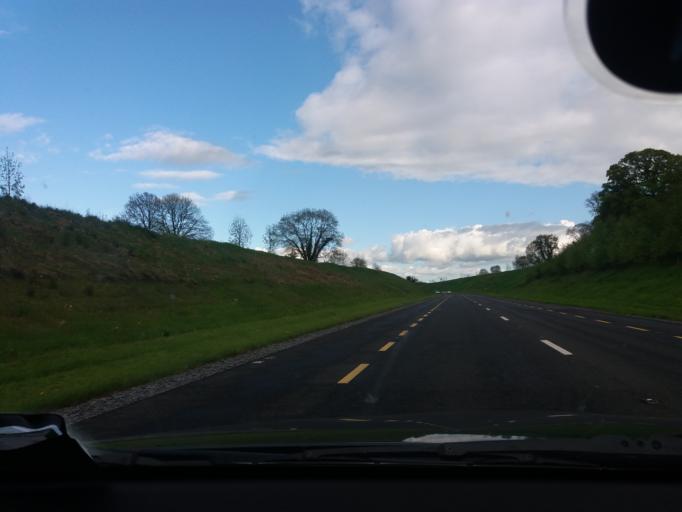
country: IE
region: Leinster
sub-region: Kilkenny
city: Kilkenny
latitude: 52.6481
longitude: -7.1904
